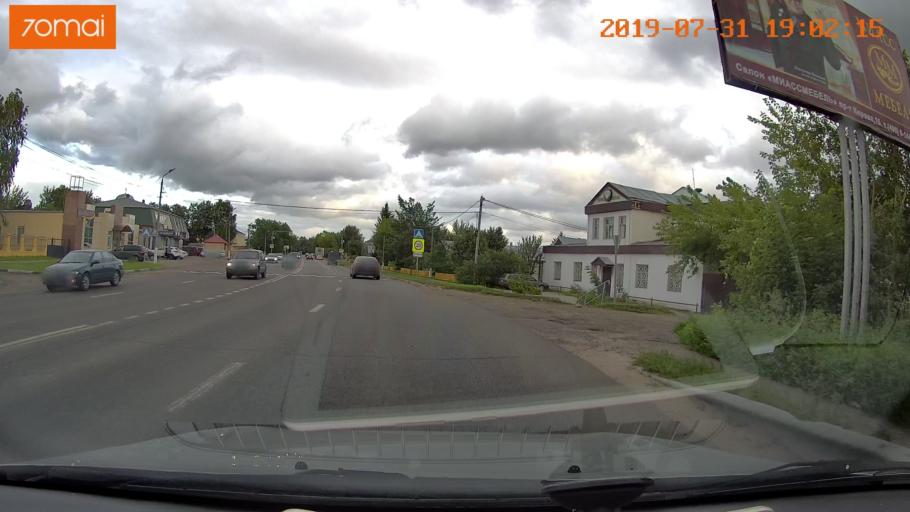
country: RU
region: Moskovskaya
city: Raduzhnyy
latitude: 55.1209
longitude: 38.7313
